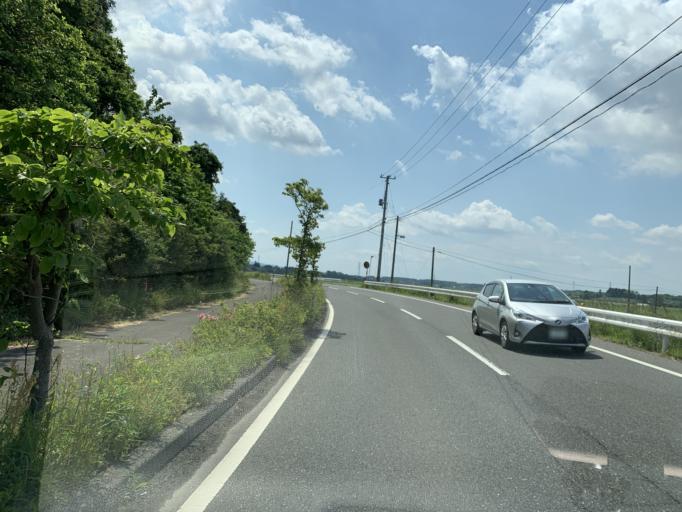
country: JP
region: Miyagi
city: Furukawa
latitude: 38.6704
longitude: 140.9940
